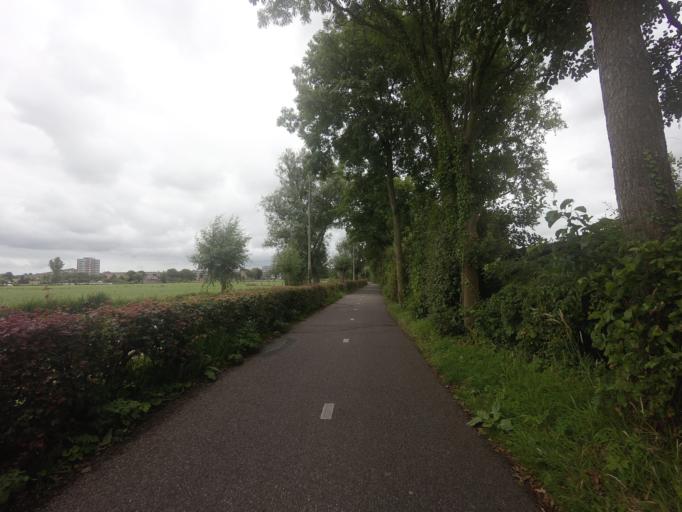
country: NL
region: North Holland
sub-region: Gemeente Bloemendaal
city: Bloemendaal
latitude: 52.4160
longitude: 4.6351
